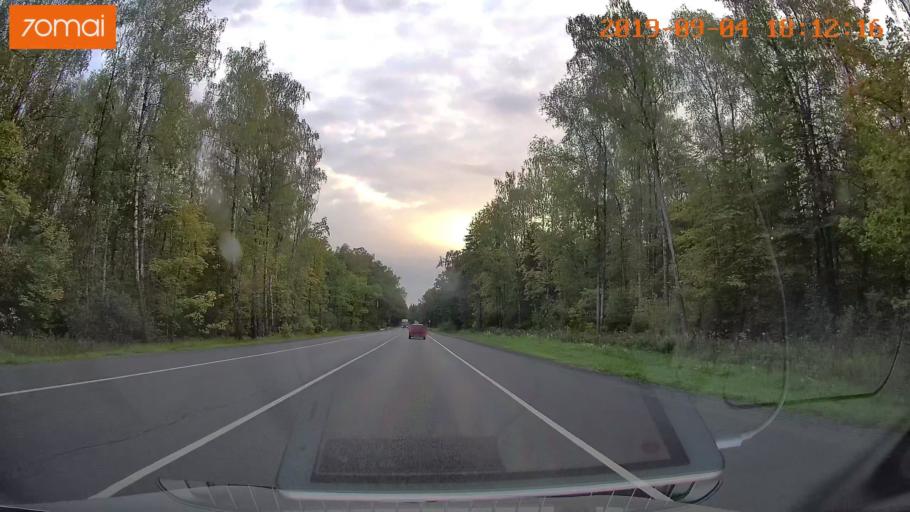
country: RU
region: Moskovskaya
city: Lopatinskiy
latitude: 55.3716
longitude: 38.7444
